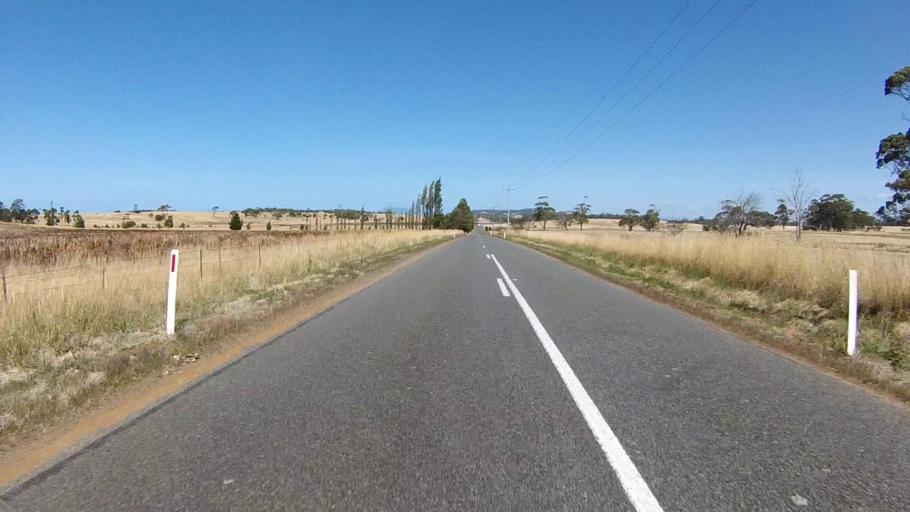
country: AU
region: Tasmania
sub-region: Sorell
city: Sorell
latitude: -42.2693
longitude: 148.0037
